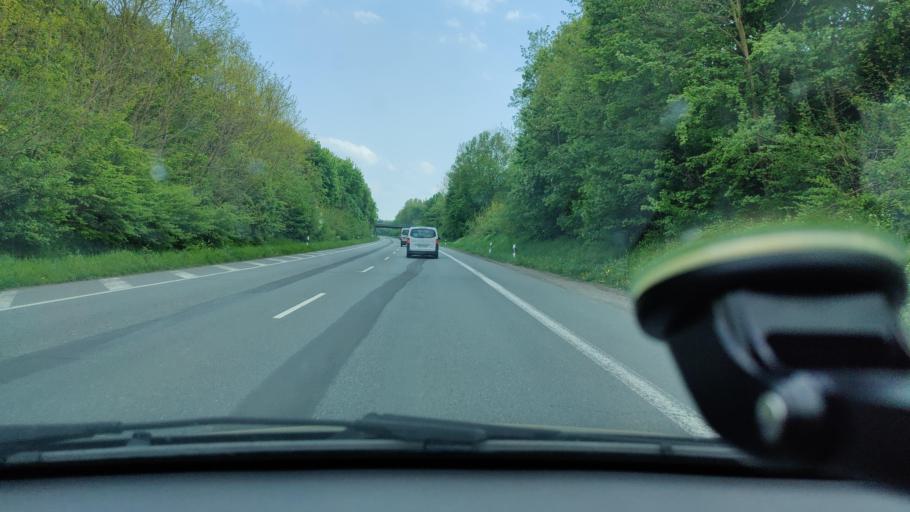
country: DE
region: North Rhine-Westphalia
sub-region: Regierungsbezirk Munster
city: Telgte
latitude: 51.9862
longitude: 7.8094
